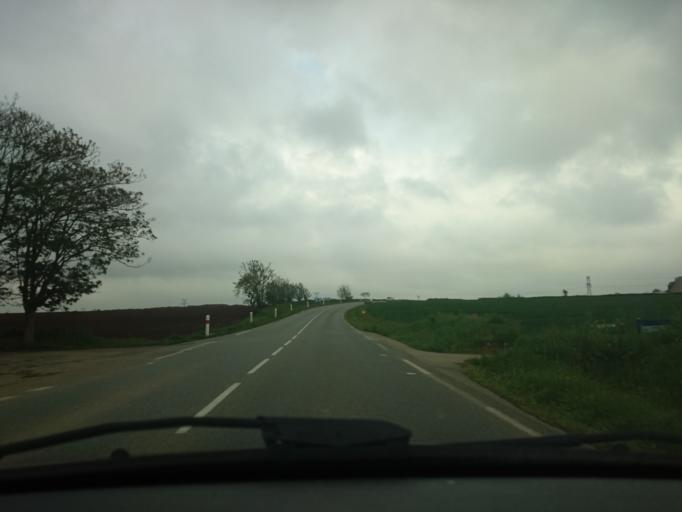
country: FR
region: Brittany
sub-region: Departement du Finistere
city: Lanrivoare
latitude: 48.4557
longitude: -4.6265
